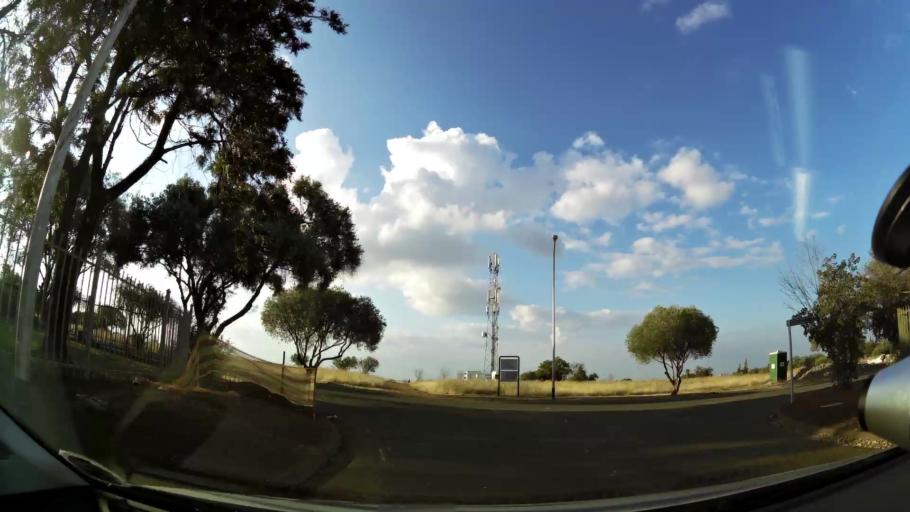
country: ZA
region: Orange Free State
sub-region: Mangaung Metropolitan Municipality
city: Bloemfontein
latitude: -29.1521
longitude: 26.1814
